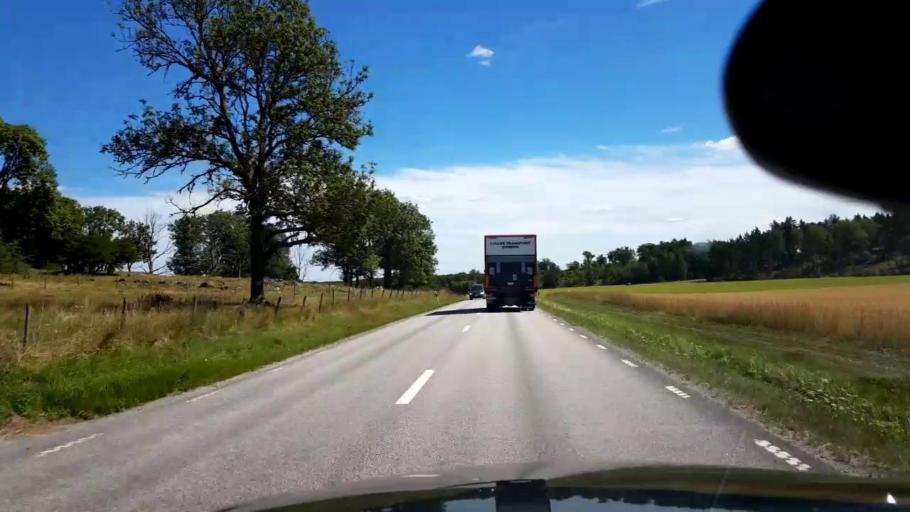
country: SE
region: Stockholm
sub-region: Sigtuna Kommun
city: Sigtuna
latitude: 59.6587
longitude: 17.6835
